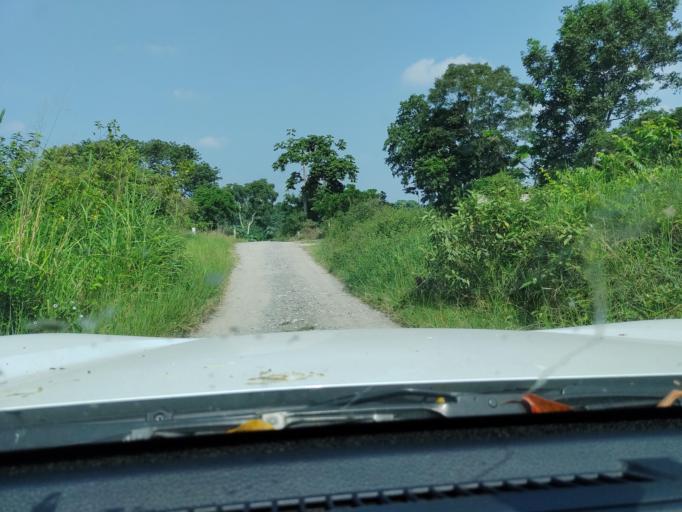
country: MX
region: Veracruz
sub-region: Martinez de la Torre
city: El Progreso
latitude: 20.0744
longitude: -97.0089
